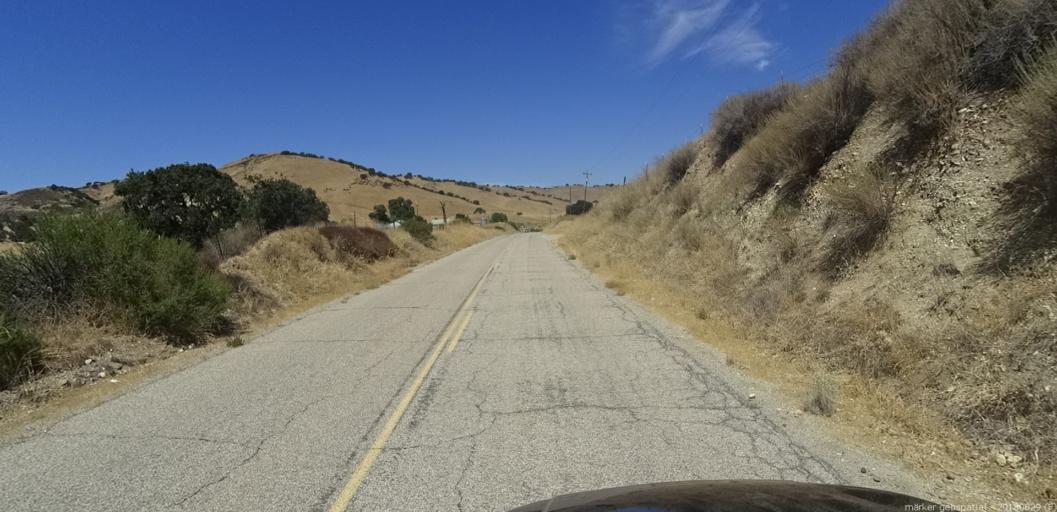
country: US
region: California
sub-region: San Luis Obispo County
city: Lake Nacimiento
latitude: 35.8045
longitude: -120.8553
